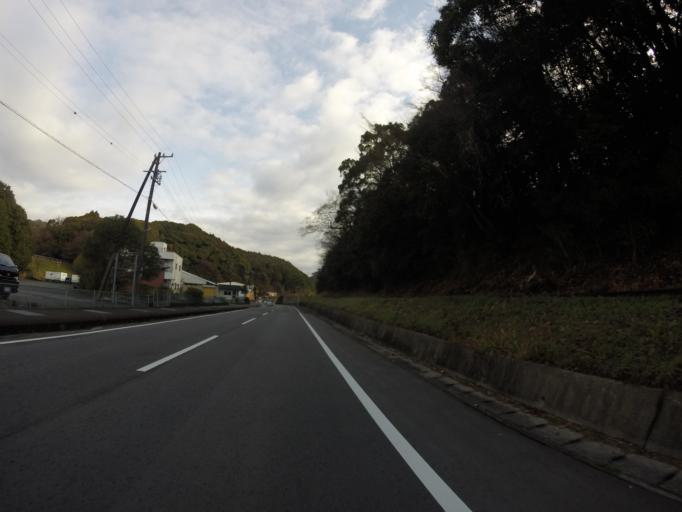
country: JP
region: Shizuoka
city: Hamakita
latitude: 34.8235
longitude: 137.7145
